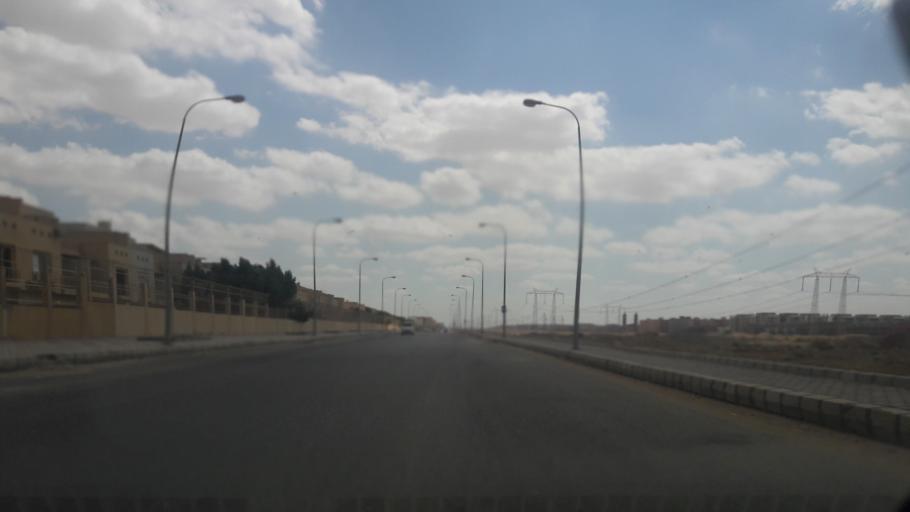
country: EG
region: Al Jizah
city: Madinat Sittah Uktubar
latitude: 29.9425
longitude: 31.0595
